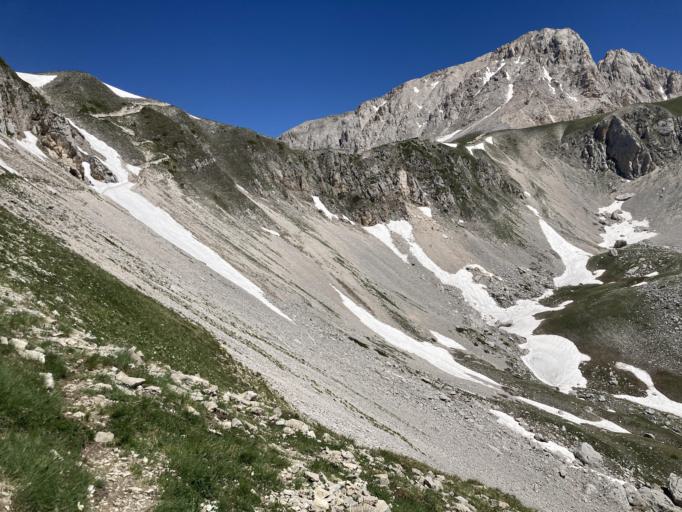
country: IT
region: Abruzzo
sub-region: Provincia di Teramo
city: Pietracamela
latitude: 42.4513
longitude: 13.5604
